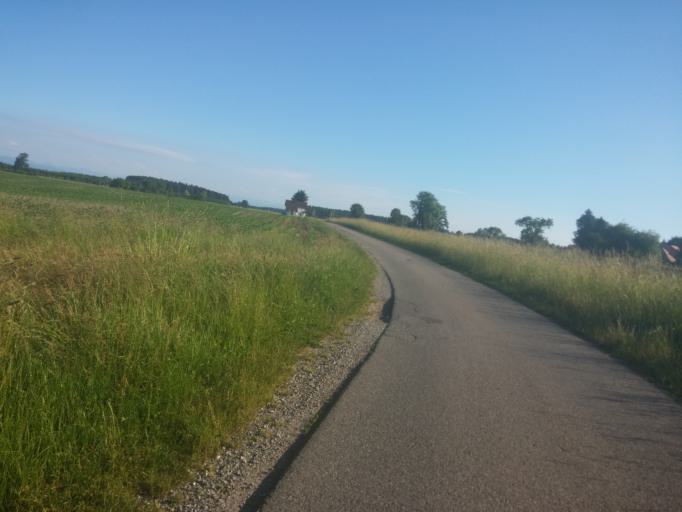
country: DE
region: Baden-Wuerttemberg
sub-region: Tuebingen Region
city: Kisslegg
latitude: 47.7773
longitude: 9.8709
